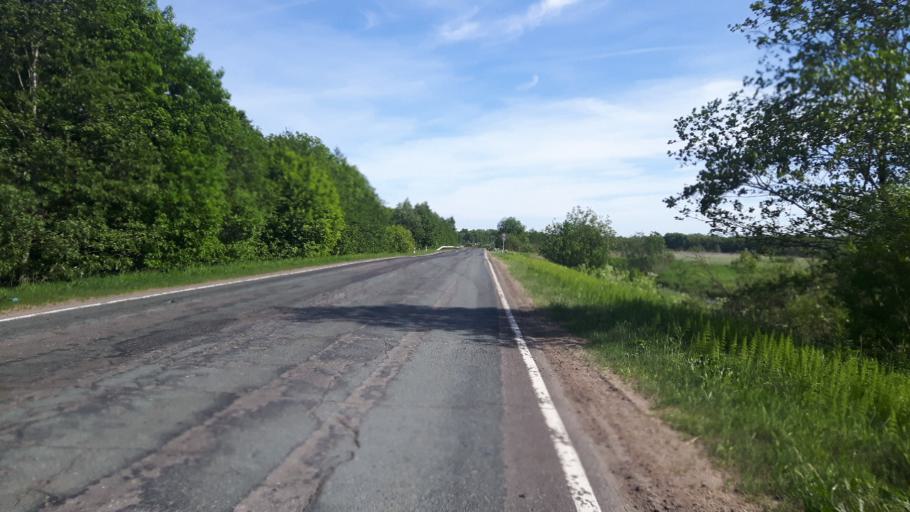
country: RU
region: Leningrad
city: Ivangorod
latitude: 59.4179
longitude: 28.3241
